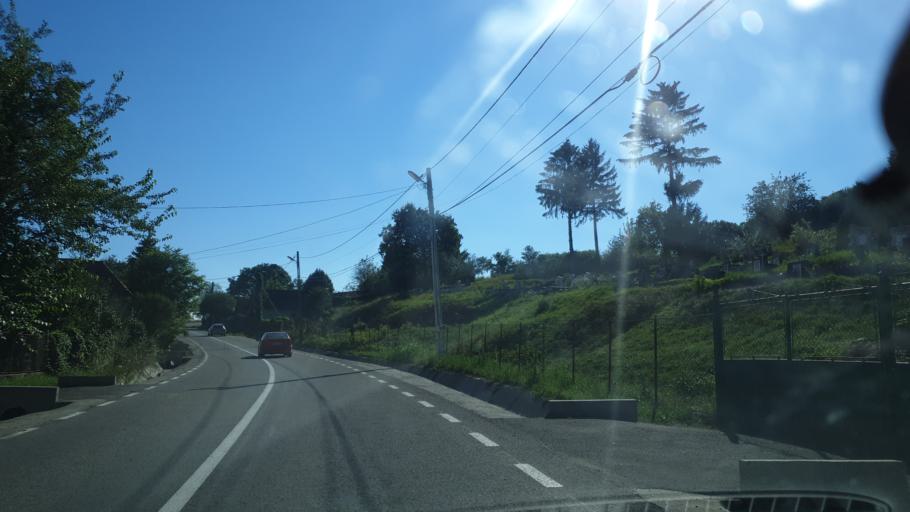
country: RO
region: Covasna
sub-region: Comuna Ilieni
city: Ilieni
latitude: 45.7906
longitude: 25.7654
